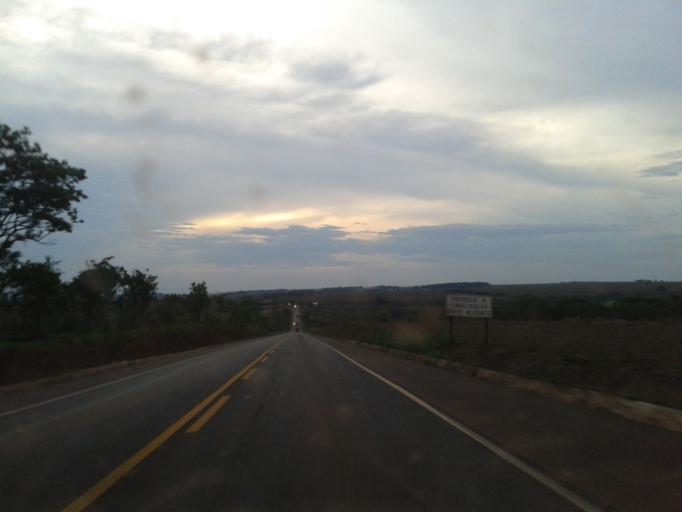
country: BR
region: Goias
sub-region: Santa Helena De Goias
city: Santa Helena de Goias
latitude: -17.8805
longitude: -50.7011
